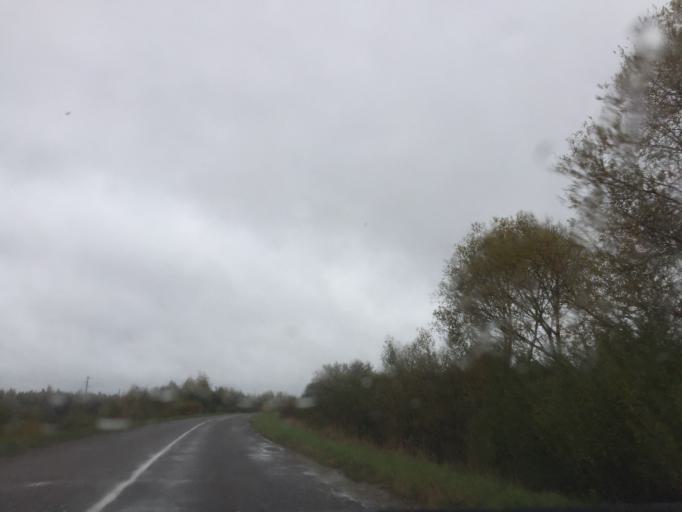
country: LV
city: Tireli
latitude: 56.8113
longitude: 23.5769
